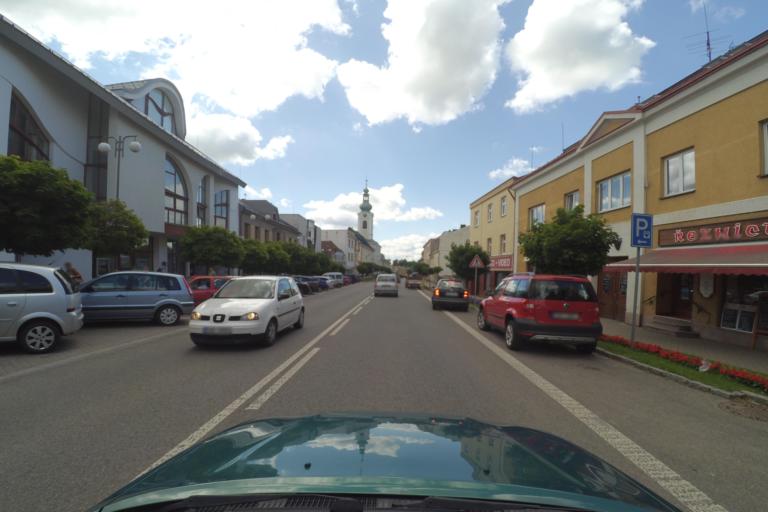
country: CZ
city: Nove Mesto nad Metuji
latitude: 50.3499
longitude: 16.1506
